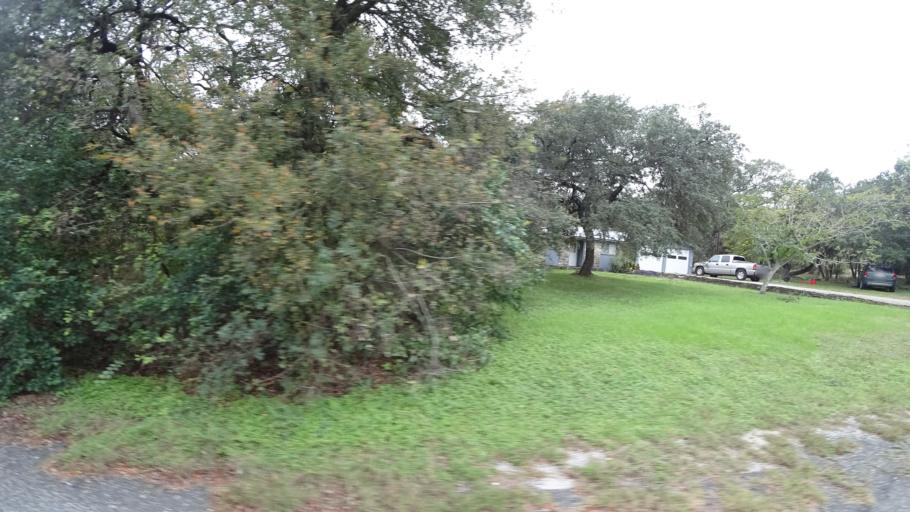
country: US
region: Texas
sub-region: Travis County
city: Barton Creek
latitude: 30.2329
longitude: -97.9004
